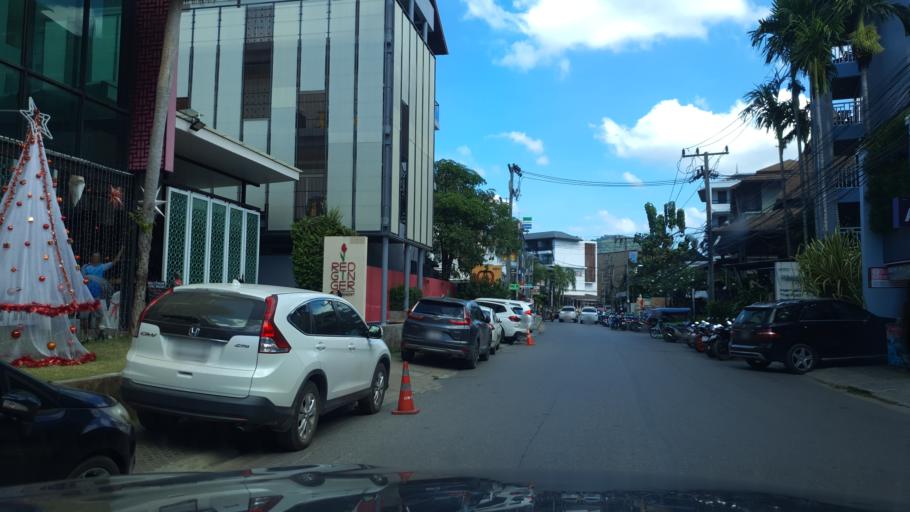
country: TH
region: Phangnga
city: Ban Ao Nang
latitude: 8.0393
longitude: 98.8174
